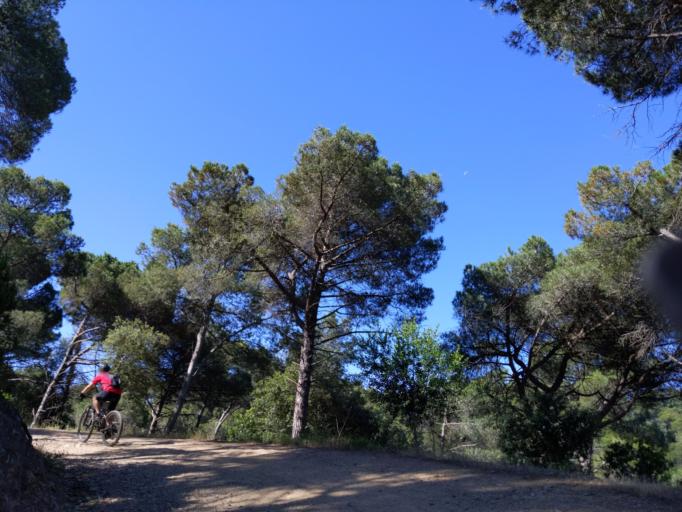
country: ES
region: Catalonia
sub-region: Provincia de Barcelona
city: Nou Barris
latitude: 41.4496
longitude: 2.1522
